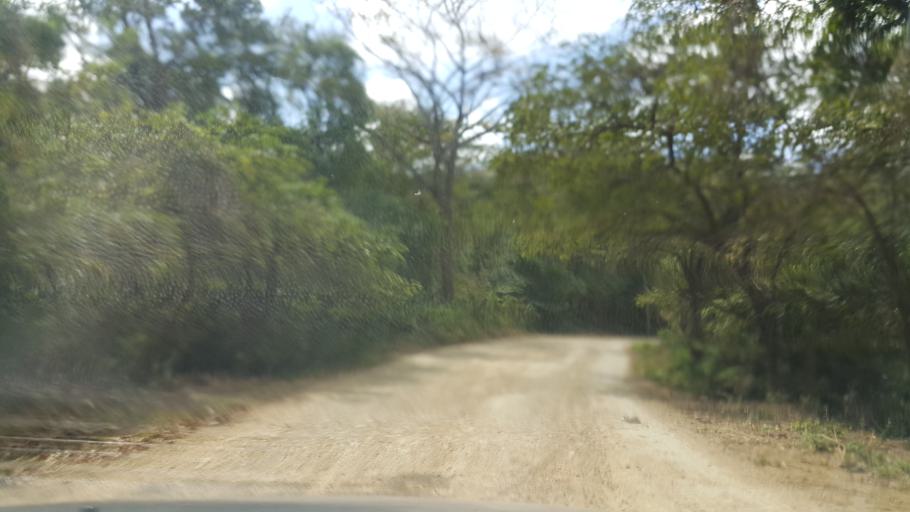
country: NI
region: Rivas
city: San Juan del Sur
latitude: 11.3021
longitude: -85.8593
